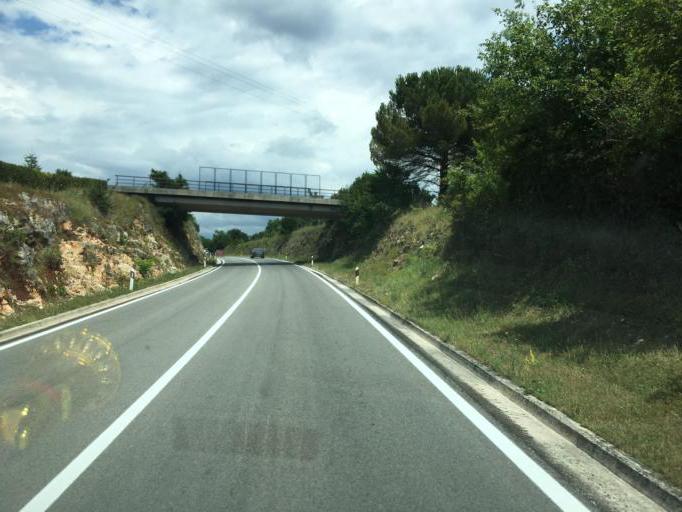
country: HR
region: Istarska
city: Karojba
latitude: 45.2183
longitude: 13.8340
